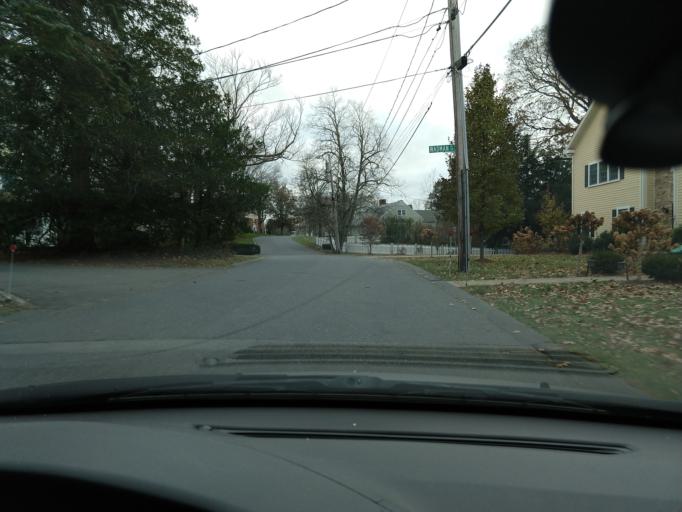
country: US
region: Massachusetts
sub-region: Middlesex County
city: Lexington
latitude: 42.4522
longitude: -71.2279
